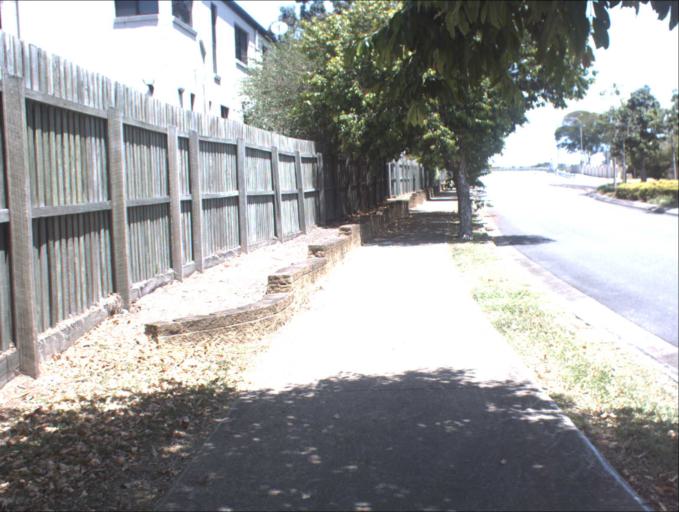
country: AU
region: Queensland
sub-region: Logan
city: Slacks Creek
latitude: -27.6409
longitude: 153.1459
